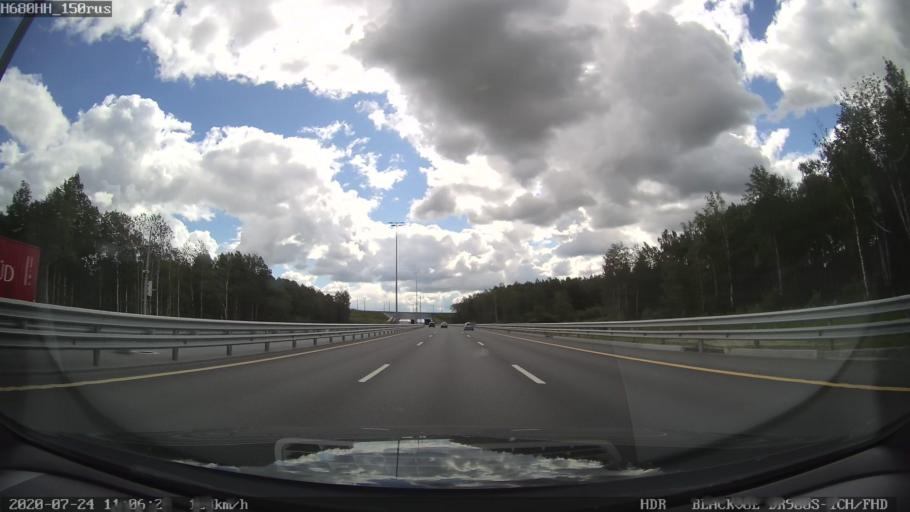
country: RU
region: St.-Petersburg
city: Shushary
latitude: 59.7620
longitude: 30.3773
